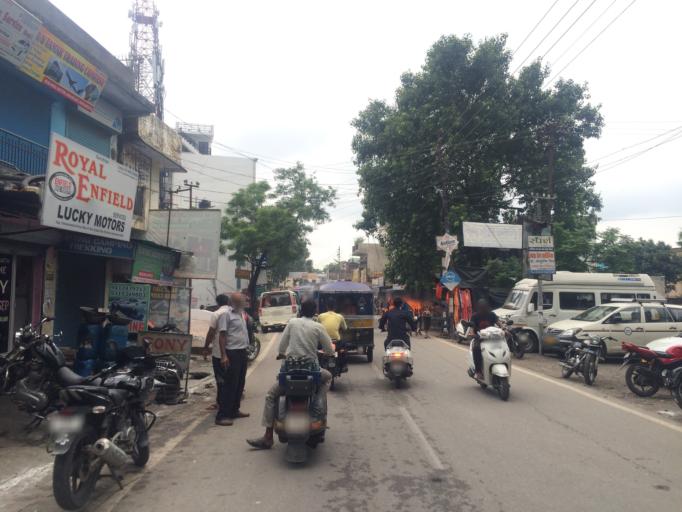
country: IN
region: Uttarakhand
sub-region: Dehradun
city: Rishikesh
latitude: 30.1154
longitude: 78.3031
